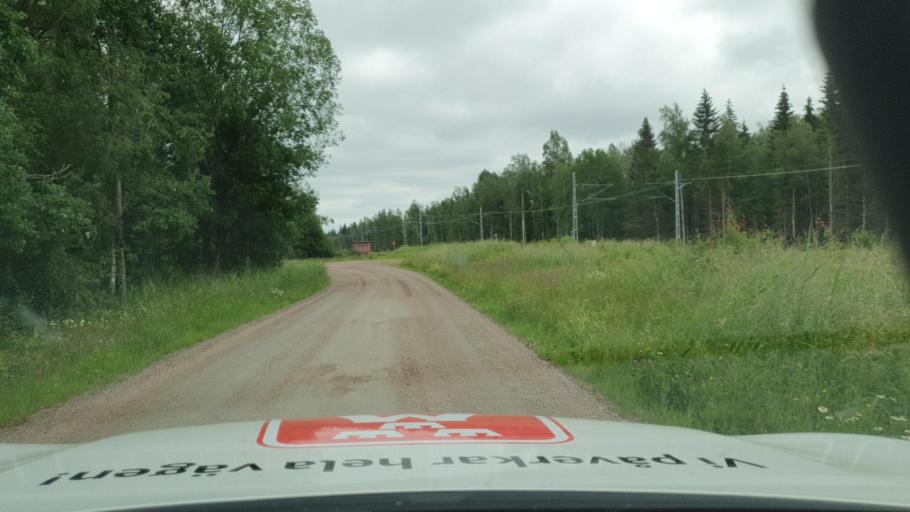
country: SE
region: Vaermland
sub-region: Filipstads Kommun
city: Filipstad
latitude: 59.5989
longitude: 13.9681
